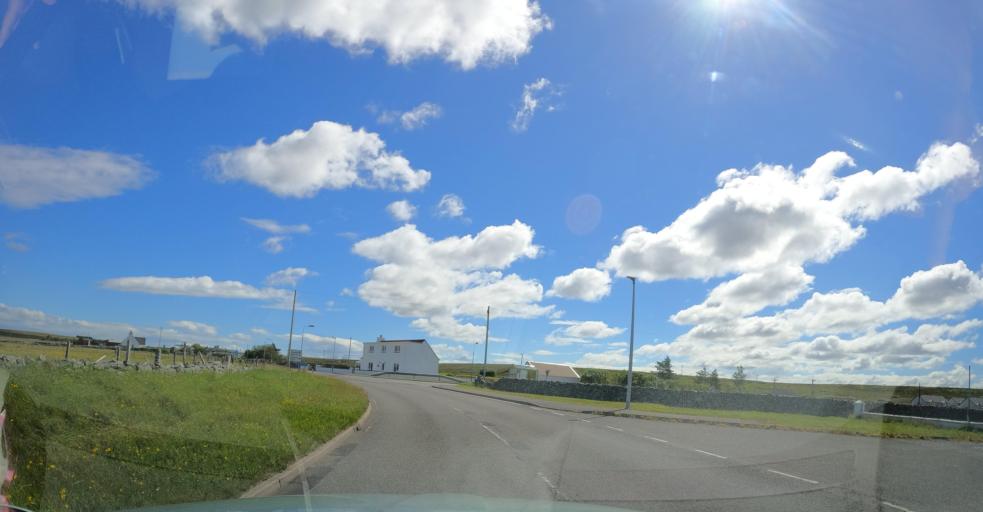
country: GB
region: Scotland
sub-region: Eilean Siar
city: Isle of Lewis
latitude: 58.3493
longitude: -6.5193
